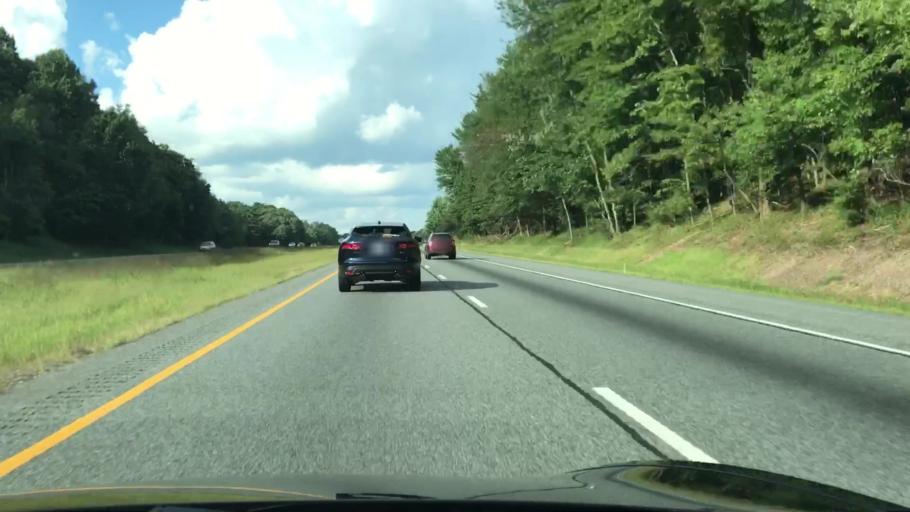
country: US
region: Pennsylvania
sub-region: York County
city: New Freedom
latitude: 39.6706
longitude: -76.6498
